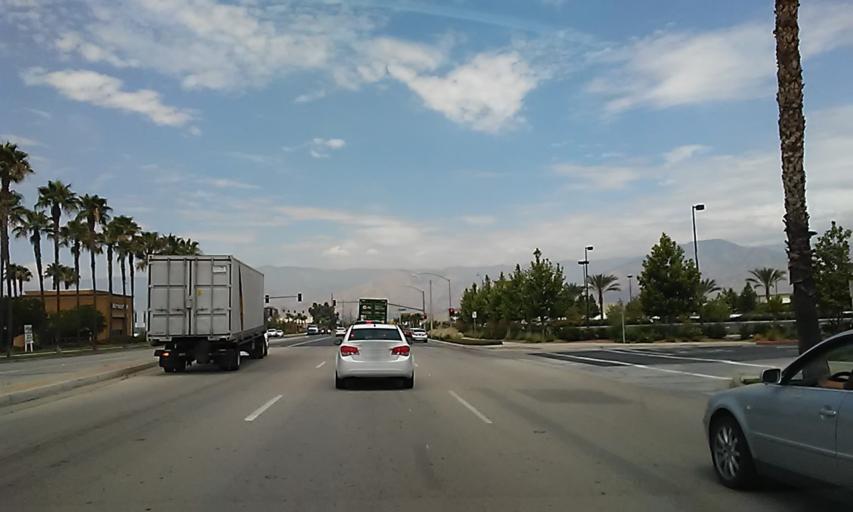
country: US
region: California
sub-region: San Bernardino County
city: Redlands
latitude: 34.0727
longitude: -117.2086
